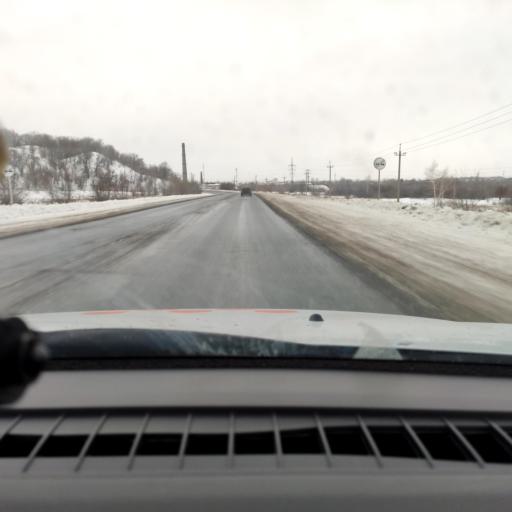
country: RU
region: Samara
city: Chapayevsk
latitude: 52.9322
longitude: 49.7166
